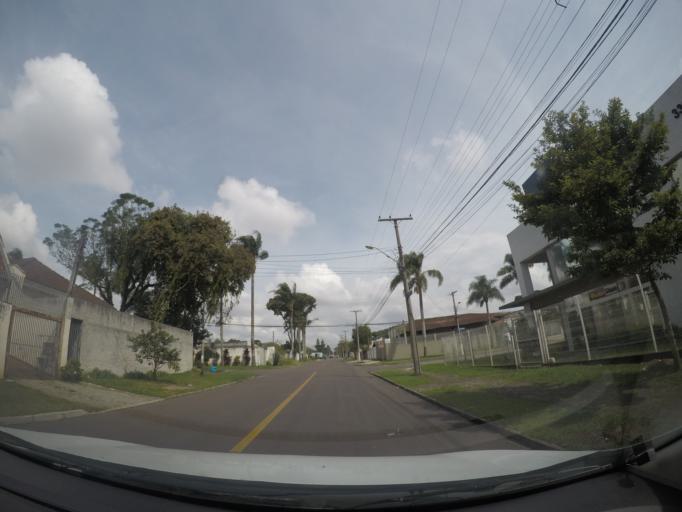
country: BR
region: Parana
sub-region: Curitiba
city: Curitiba
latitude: -25.4784
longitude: -49.2634
